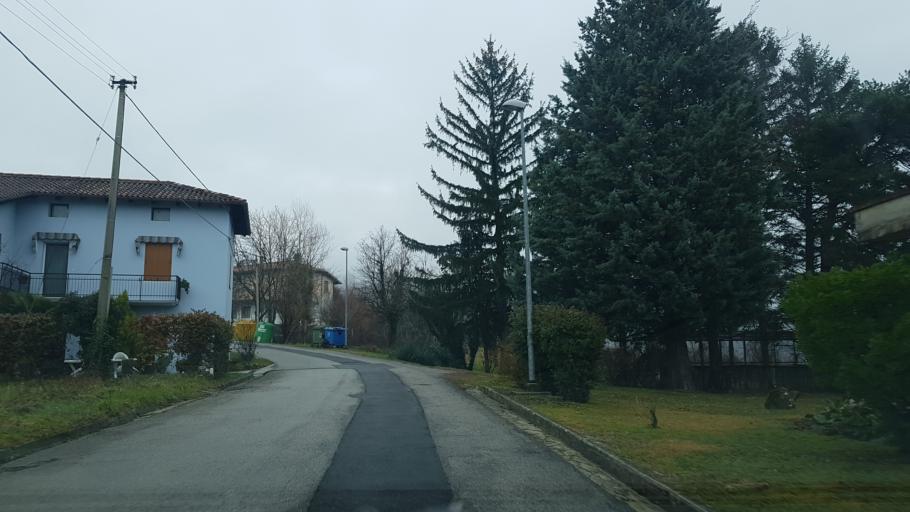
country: IT
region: Friuli Venezia Giulia
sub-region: Provincia di Udine
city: Prepotto
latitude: 46.0785
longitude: 13.4801
